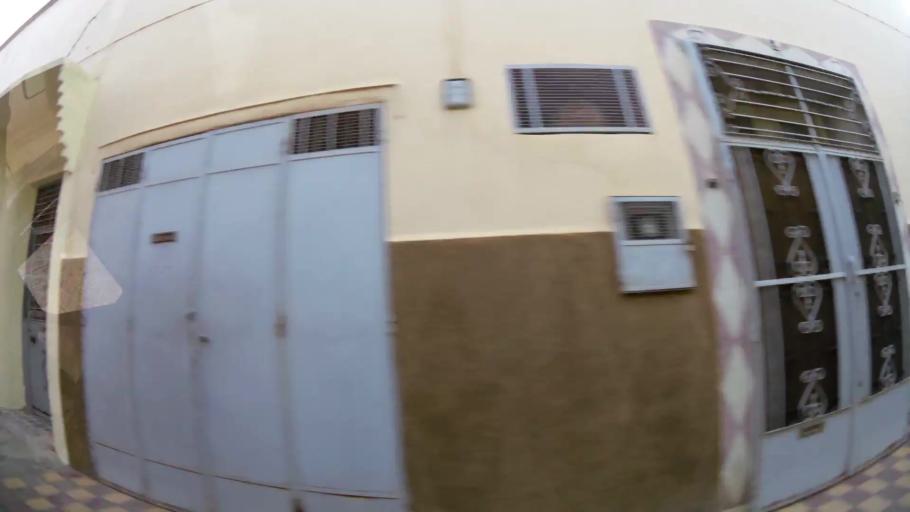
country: MA
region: Oriental
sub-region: Oujda-Angad
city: Oujda
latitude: 34.6800
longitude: -1.8886
